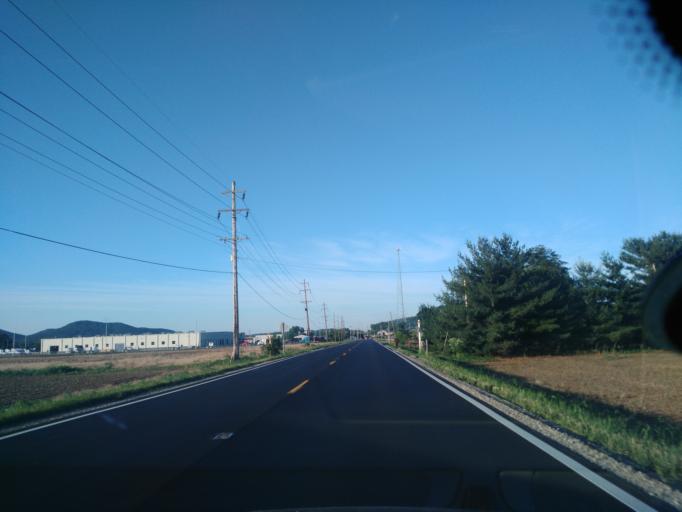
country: US
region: Ohio
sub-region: Ross County
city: Kingston
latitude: 39.4123
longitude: -82.9581
